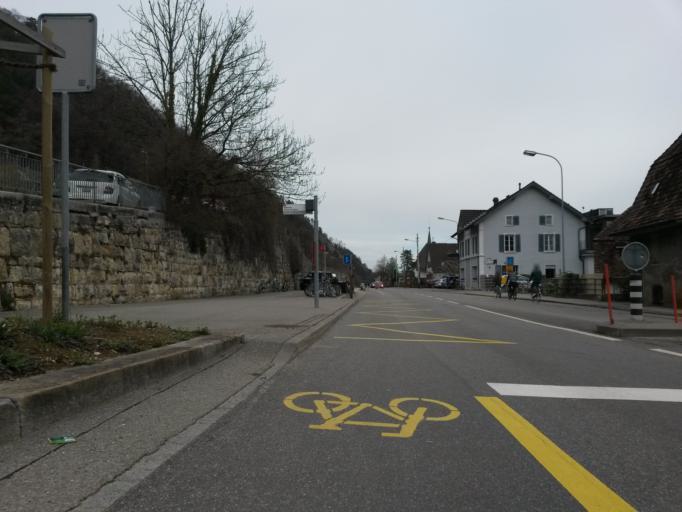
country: CH
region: Bern
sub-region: Biel/Bienne District
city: Nidau
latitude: 47.1316
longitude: 7.2214
